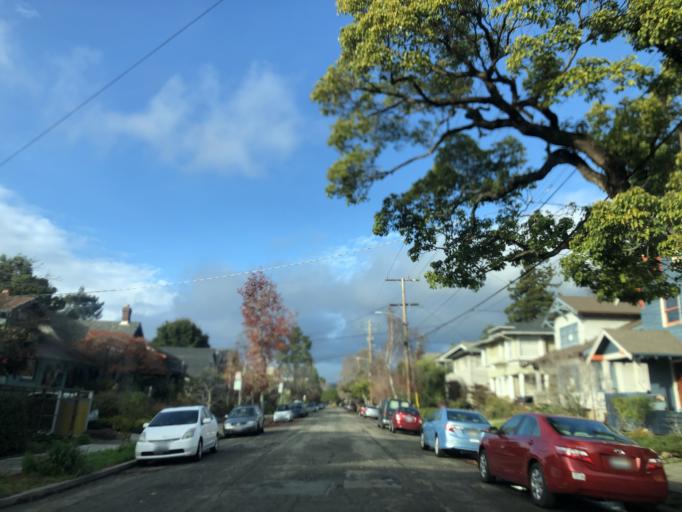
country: US
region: California
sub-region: Alameda County
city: Berkeley
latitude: 37.8514
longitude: -122.2558
